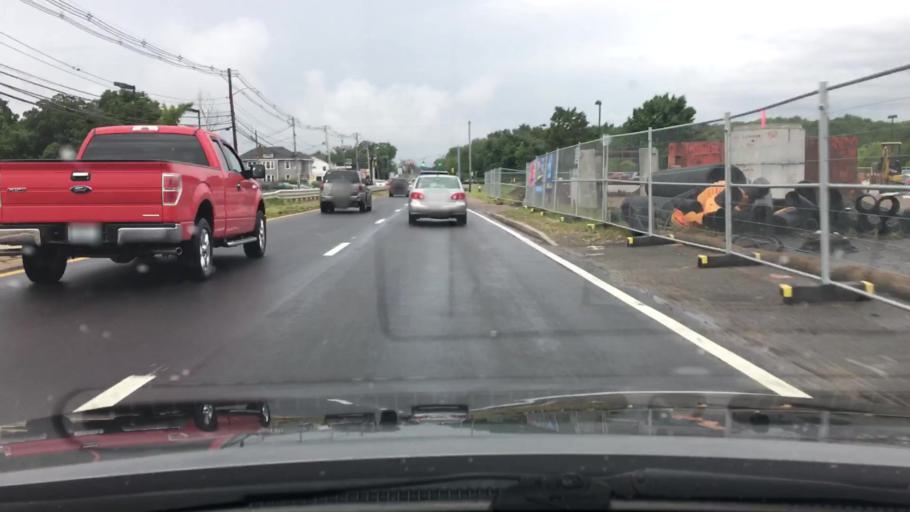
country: US
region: Massachusetts
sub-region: Norfolk County
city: Plainville
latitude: 41.9534
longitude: -71.3441
